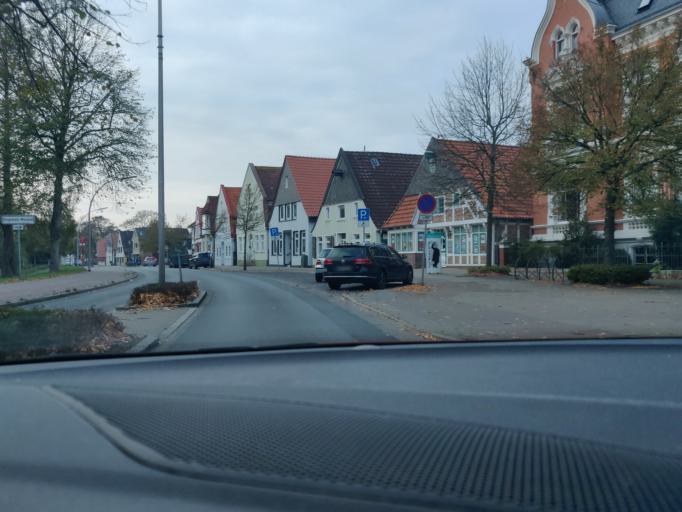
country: DE
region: Lower Saxony
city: Cuxhaven
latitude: 53.8577
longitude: 8.7006
